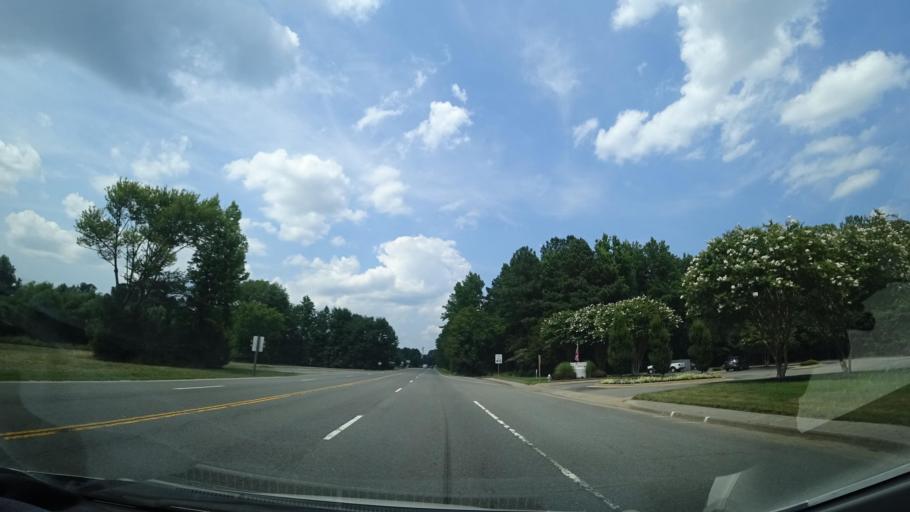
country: US
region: Virginia
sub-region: Hanover County
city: Ashland
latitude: 37.7715
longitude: -77.4687
